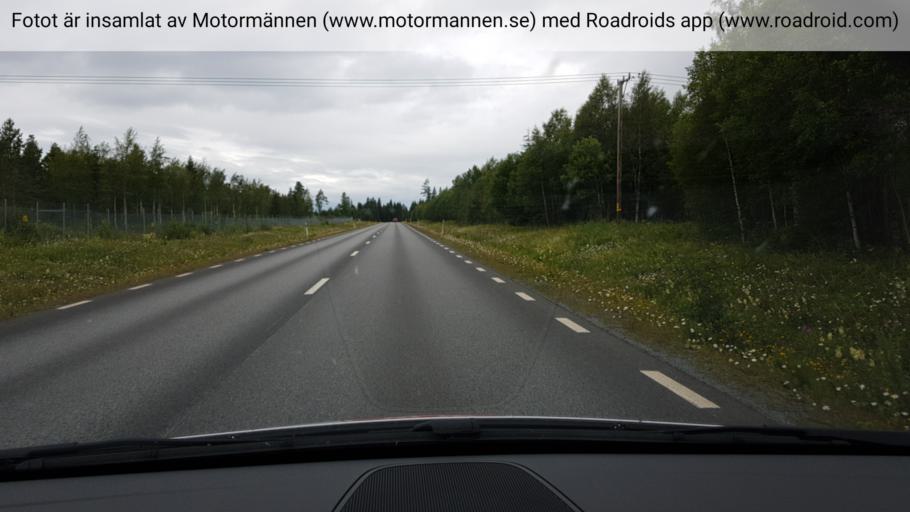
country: SE
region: Jaemtland
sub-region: Krokoms Kommun
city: Krokom
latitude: 63.2024
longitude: 14.4898
